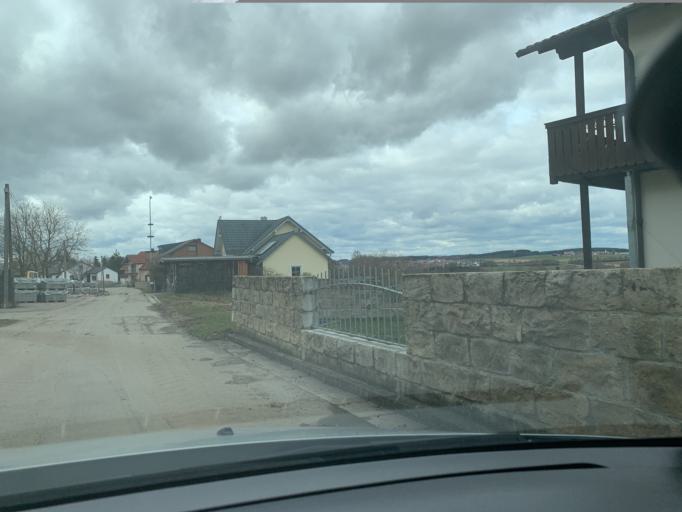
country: DE
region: Bavaria
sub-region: Lower Bavaria
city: Geisenhausen
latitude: 48.4702
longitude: 12.2788
